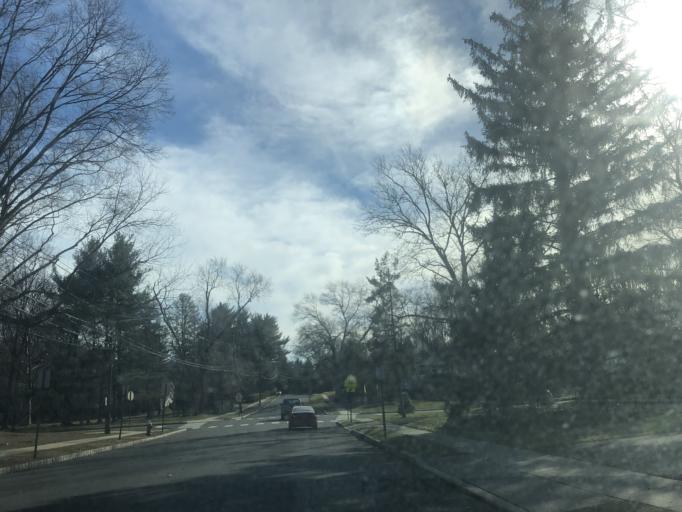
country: US
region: New Jersey
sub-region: Mercer County
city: Princeton
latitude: 40.3540
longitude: -74.6374
